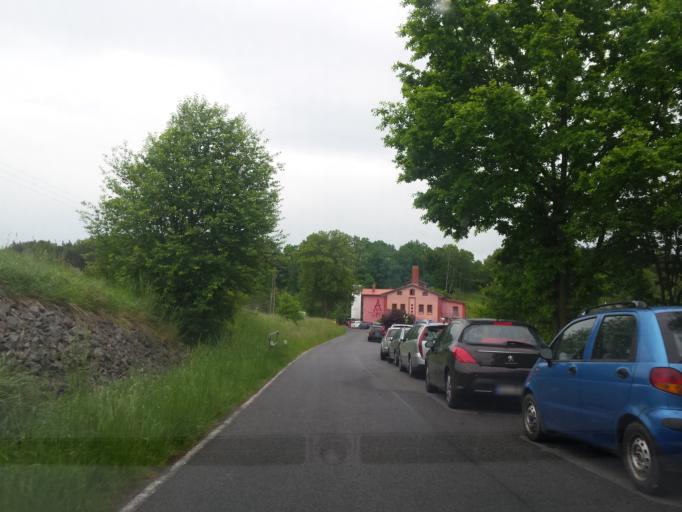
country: CZ
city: Cvikov
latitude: 50.7374
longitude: 14.6365
